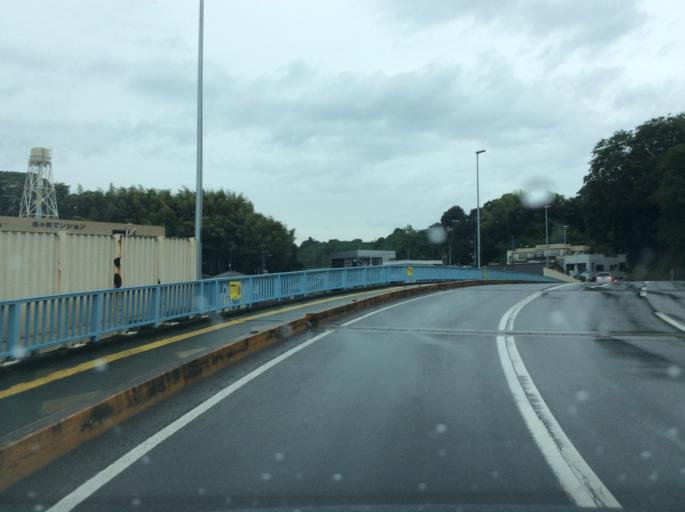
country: JP
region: Fukushima
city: Iwaki
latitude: 37.0576
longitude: 140.8884
